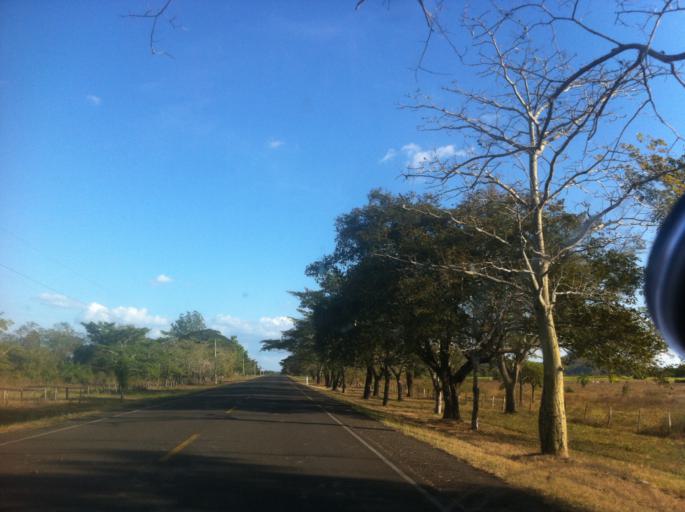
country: NI
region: Rio San Juan
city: Morrito
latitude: 11.7732
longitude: -85.0140
